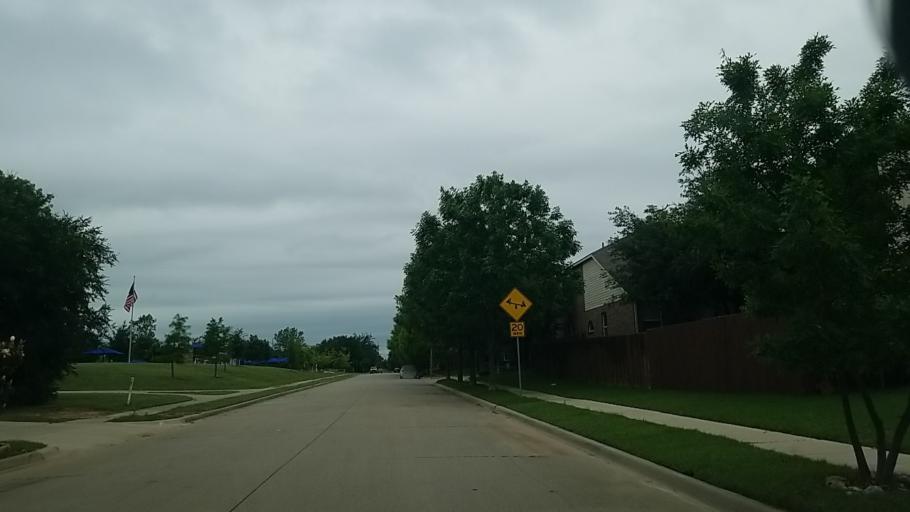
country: US
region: Texas
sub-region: Denton County
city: Corinth
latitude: 33.1674
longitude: -97.0726
